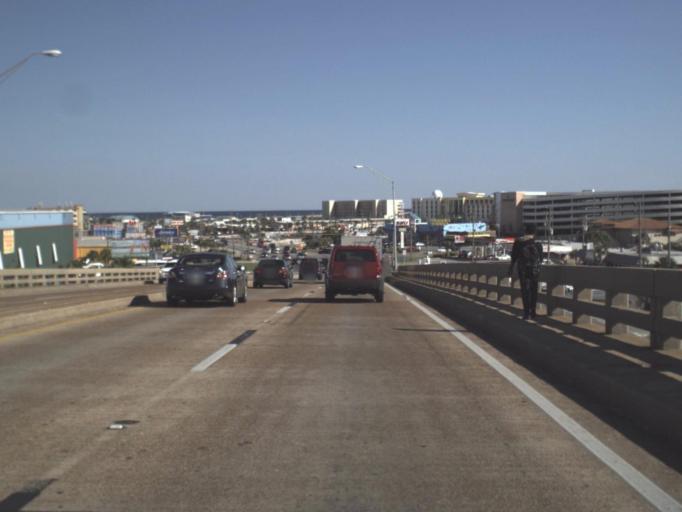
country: US
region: Florida
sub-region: Okaloosa County
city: Fort Walton Beach
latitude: 30.4002
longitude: -86.6000
